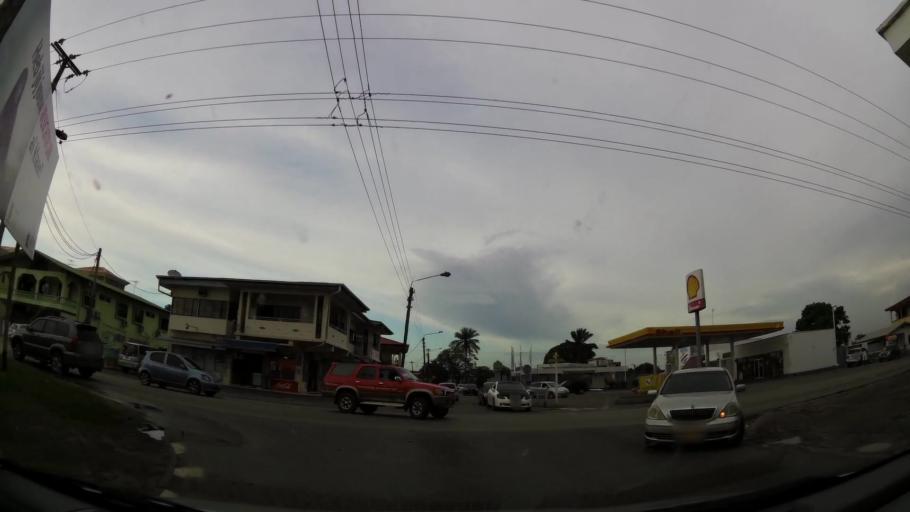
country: SR
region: Paramaribo
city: Paramaribo
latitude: 5.8244
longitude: -55.2030
